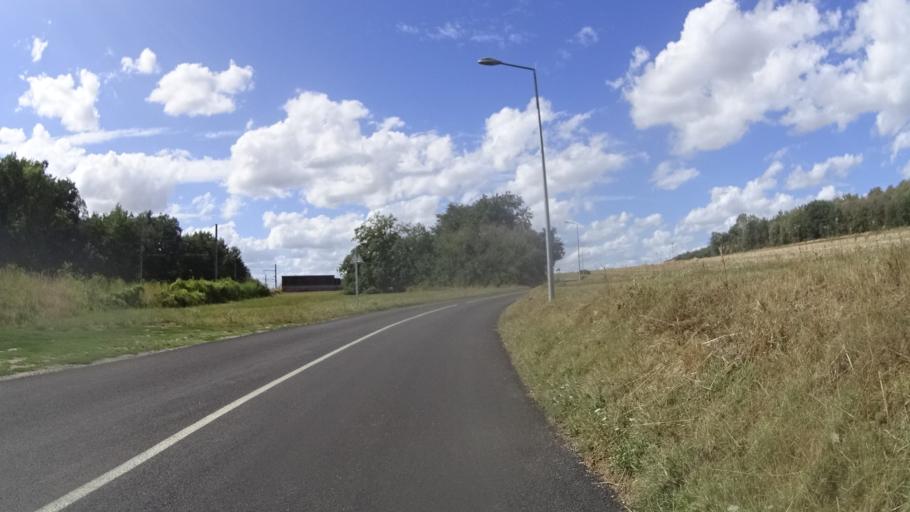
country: FR
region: Ile-de-France
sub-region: Departement de l'Essonne
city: La Ferte-Alais
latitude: 48.4549
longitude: 2.3596
